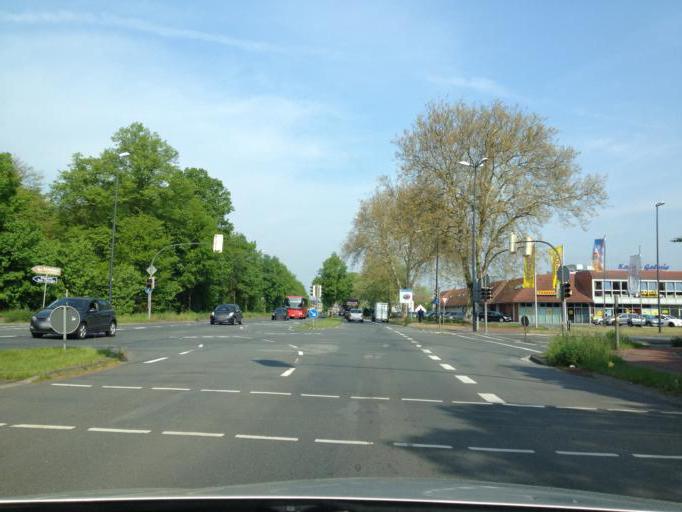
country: DE
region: North Rhine-Westphalia
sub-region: Regierungsbezirk Detmold
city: Guetersloh
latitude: 51.9007
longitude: 8.3984
